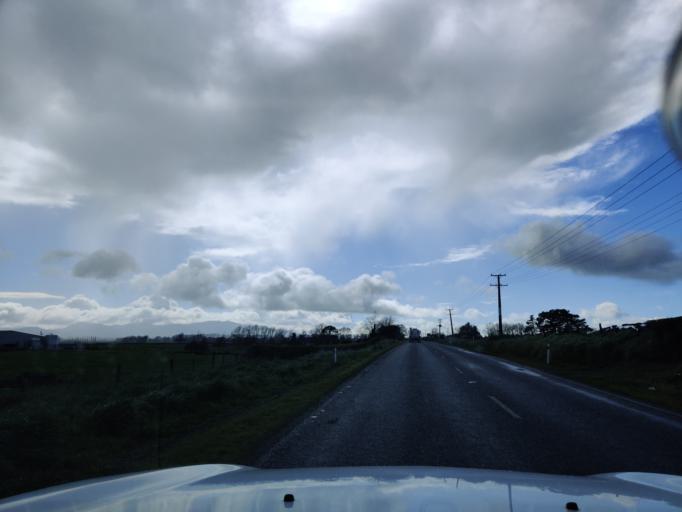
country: NZ
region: Waikato
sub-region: Waikato District
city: Ngaruawahia
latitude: -37.5741
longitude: 175.2426
